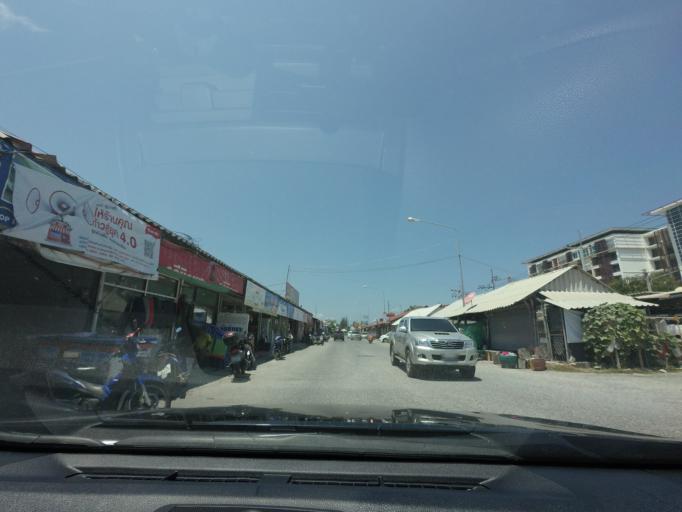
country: TH
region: Prachuap Khiri Khan
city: Hua Hin
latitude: 12.5731
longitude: 99.9532
